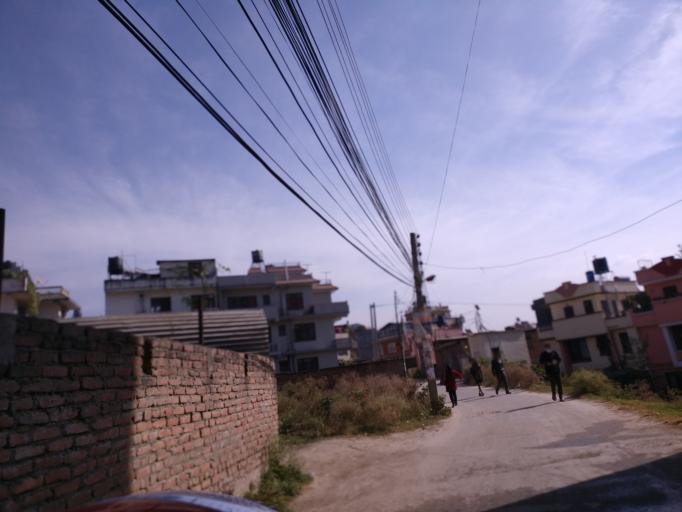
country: NP
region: Central Region
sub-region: Bagmati Zone
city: Patan
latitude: 27.6629
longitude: 85.3087
